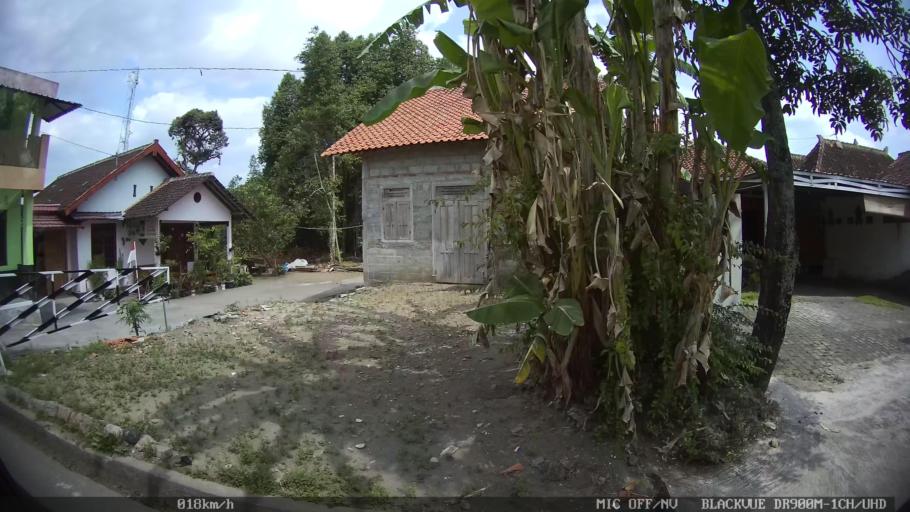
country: ID
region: Daerah Istimewa Yogyakarta
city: Kasihan
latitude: -7.8238
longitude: 110.3387
